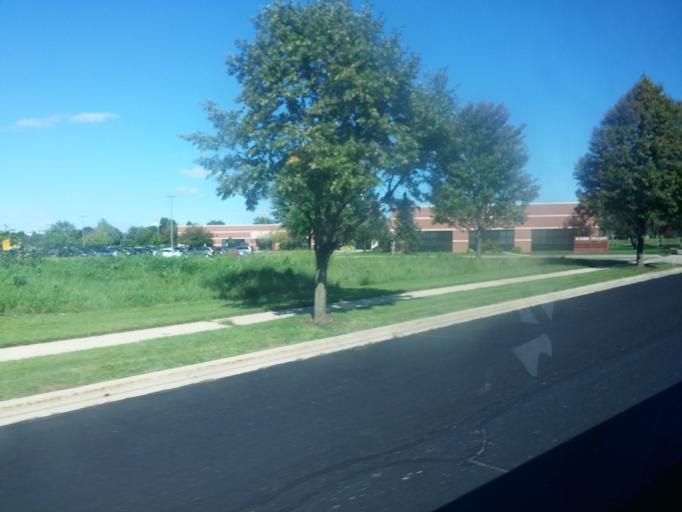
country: US
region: Wisconsin
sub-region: Dane County
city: Maple Bluff
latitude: 43.1425
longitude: -89.2948
